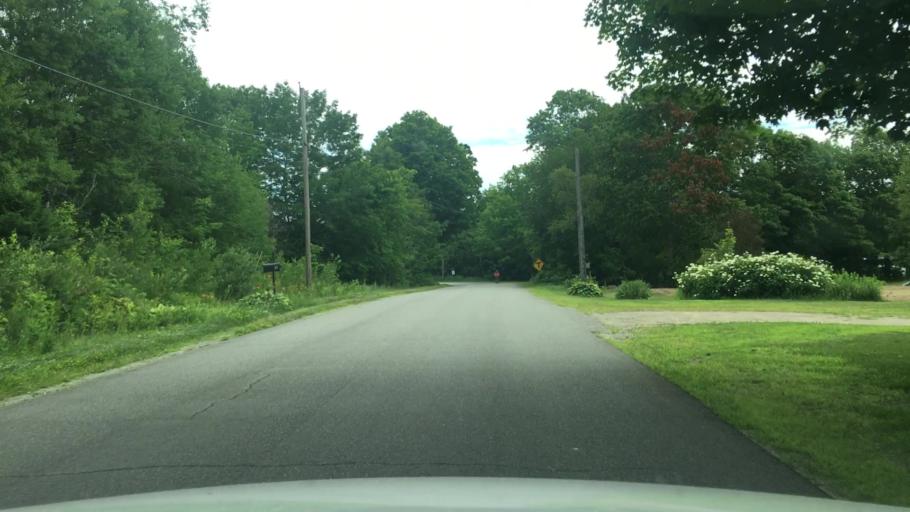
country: US
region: Maine
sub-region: Kennebec County
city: Albion
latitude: 44.4675
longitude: -69.3393
